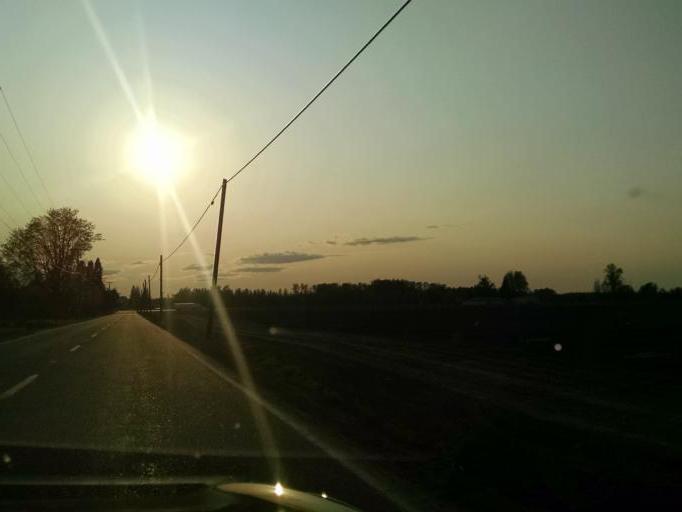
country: US
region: Washington
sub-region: Whatcom County
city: Nooksack
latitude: 48.8838
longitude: -122.3143
